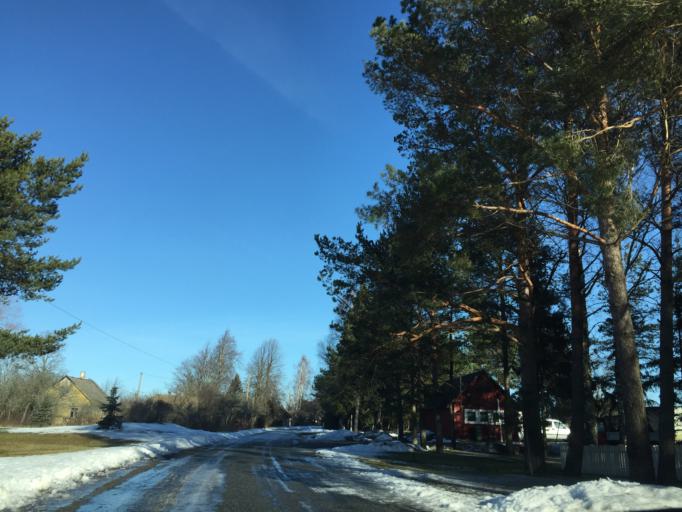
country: LV
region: Salacgrivas
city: Ainazi
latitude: 58.0823
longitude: 24.4892
